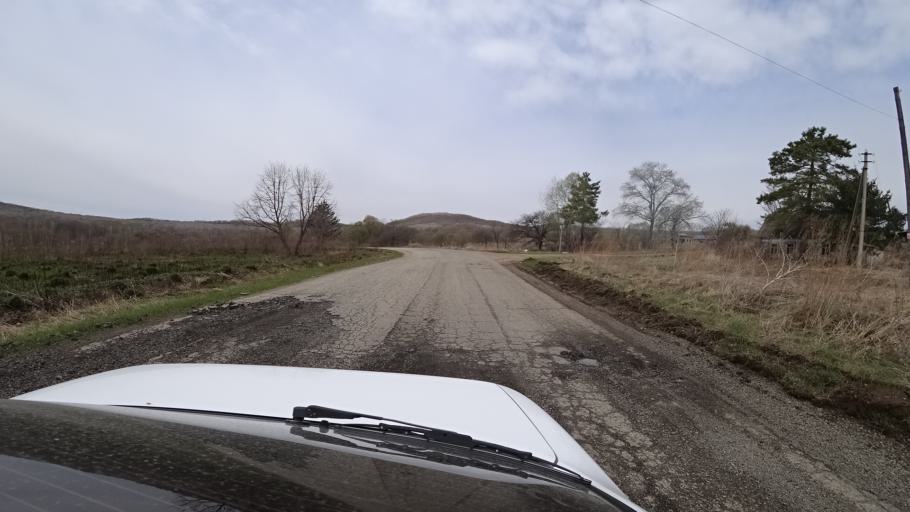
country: RU
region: Primorskiy
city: Dal'nerechensk
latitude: 45.7993
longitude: 134.1007
